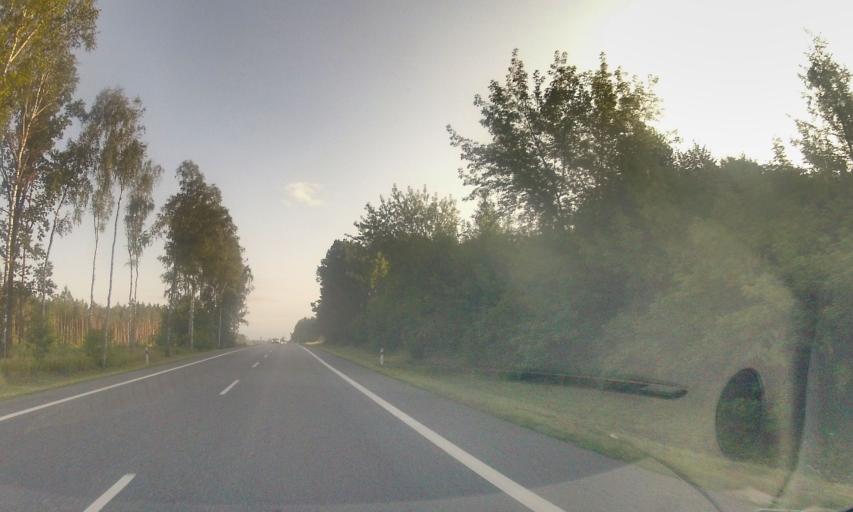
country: PL
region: Masovian Voivodeship
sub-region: Powiat mlawski
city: Strzegowo
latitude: 52.9182
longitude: 20.2863
